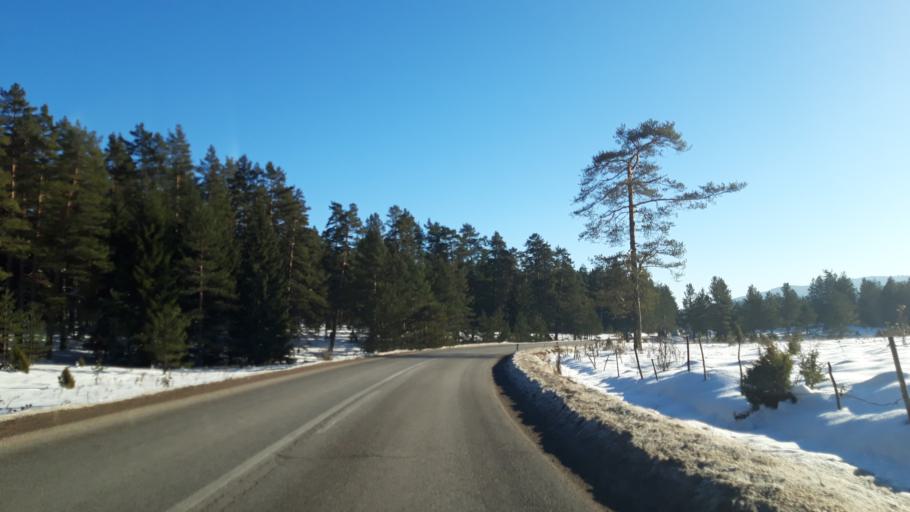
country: BA
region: Republika Srpska
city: Sokolac
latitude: 43.9168
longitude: 18.7007
